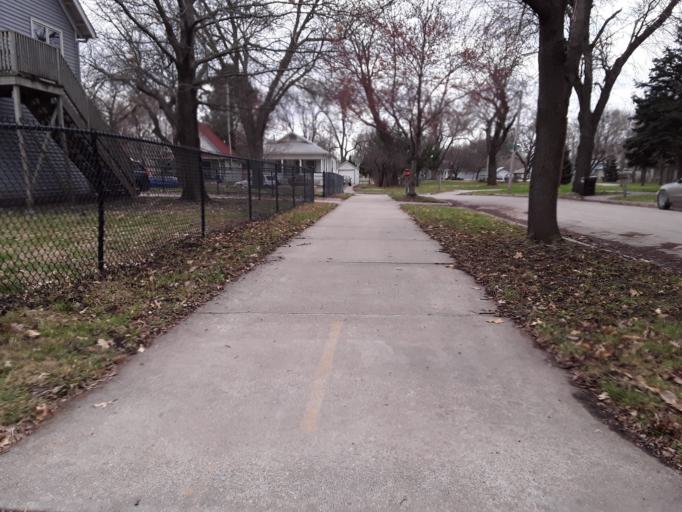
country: US
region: Nebraska
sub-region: Lancaster County
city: Lincoln
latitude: 40.8296
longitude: -96.6911
